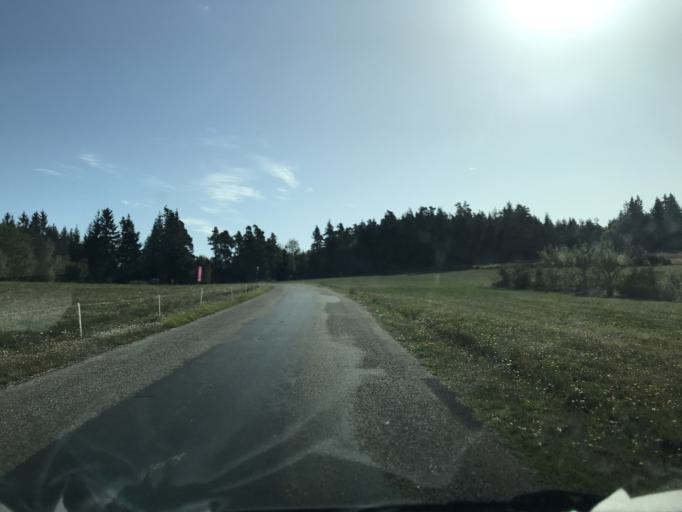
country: FR
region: Rhone-Alpes
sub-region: Departement de l'Ardeche
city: Saint-Agreve
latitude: 45.0362
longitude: 4.4414
